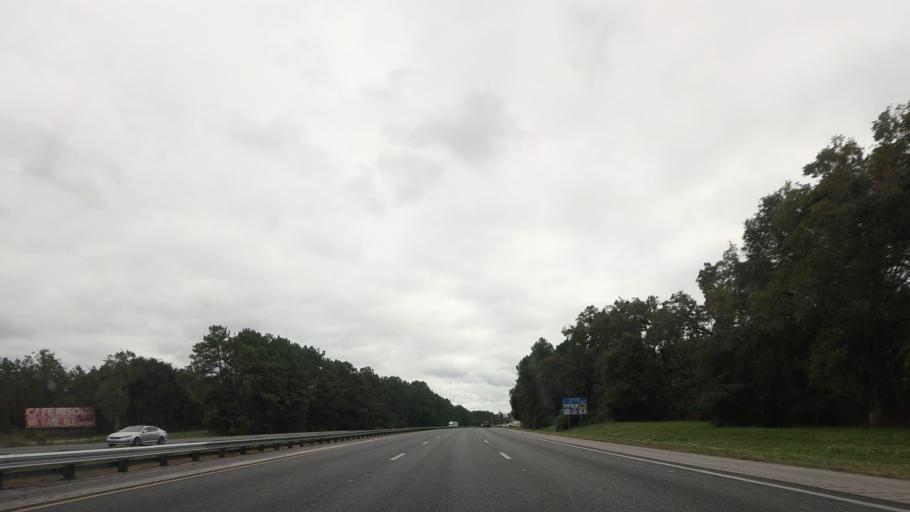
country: US
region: Florida
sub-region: Alachua County
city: High Springs
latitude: 29.8098
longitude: -82.5133
